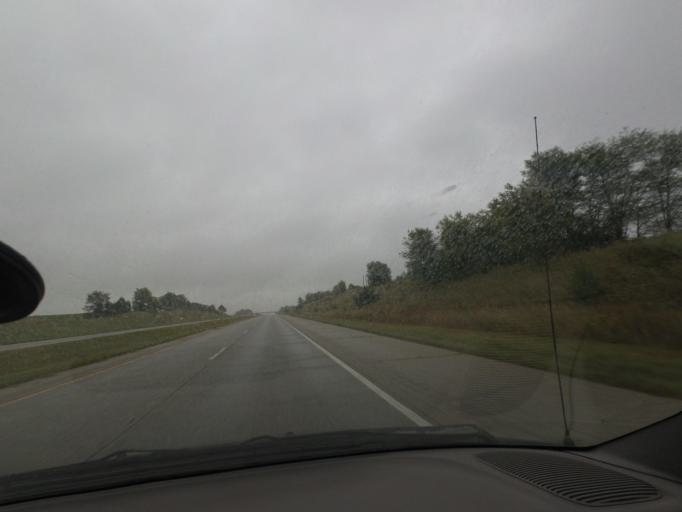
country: US
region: Illinois
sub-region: Pike County
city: Barry
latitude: 39.7075
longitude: -91.0504
